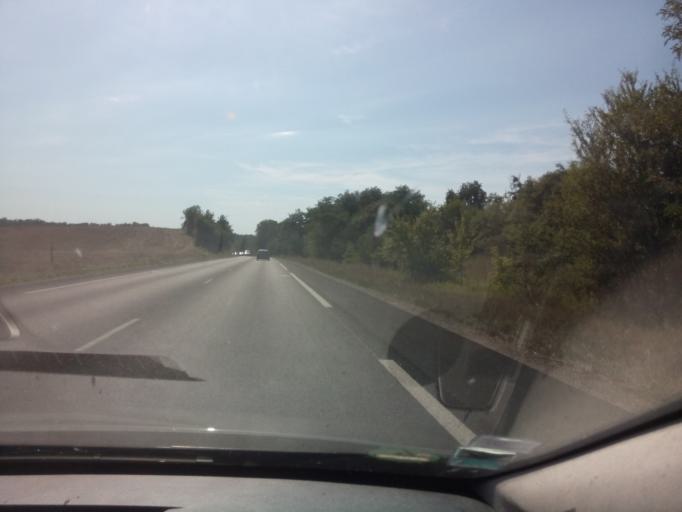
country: FR
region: Alsace
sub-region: Departement du Bas-Rhin
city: Surbourg
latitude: 48.9015
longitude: 7.8548
